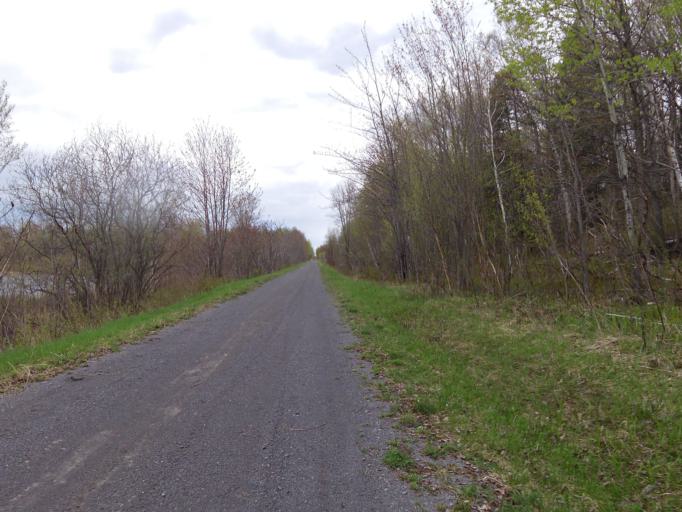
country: CA
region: Quebec
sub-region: Outaouais
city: Papineauville
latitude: 45.5175
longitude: -74.9487
